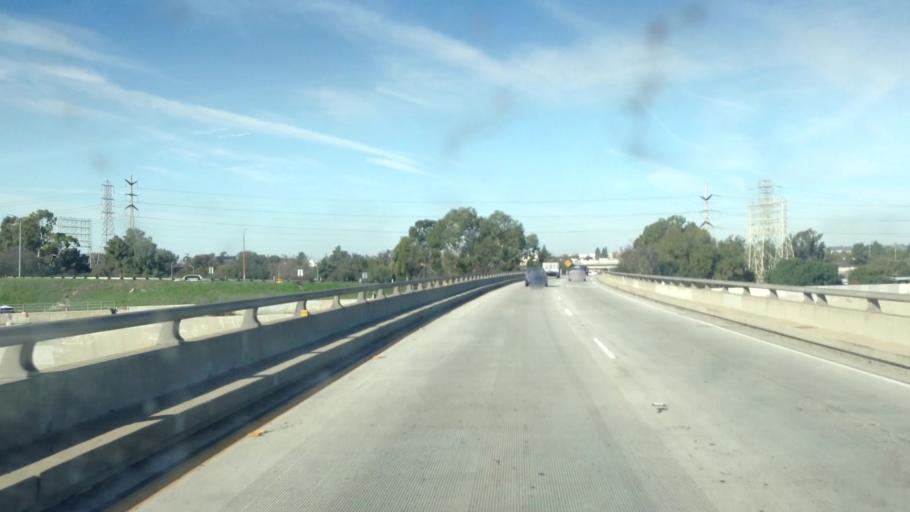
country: US
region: California
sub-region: Los Angeles County
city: Signal Hill
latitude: 33.8265
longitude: -118.2046
